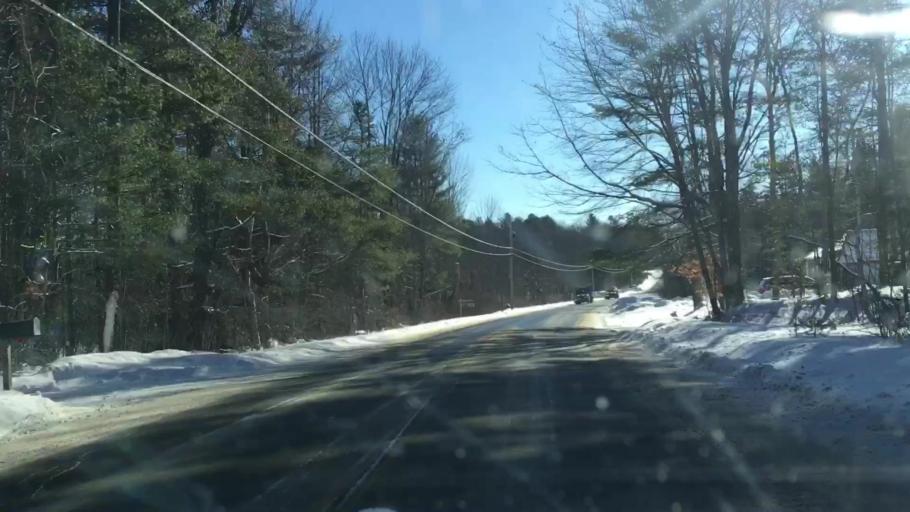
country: US
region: Maine
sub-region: Sagadahoc County
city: Topsham
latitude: 43.9242
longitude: -70.0444
